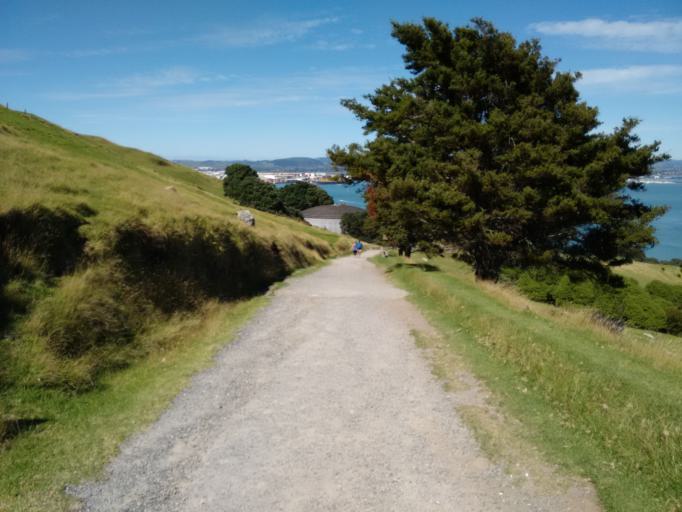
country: NZ
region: Bay of Plenty
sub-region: Tauranga City
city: Tauranga
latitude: -37.6325
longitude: 176.1692
